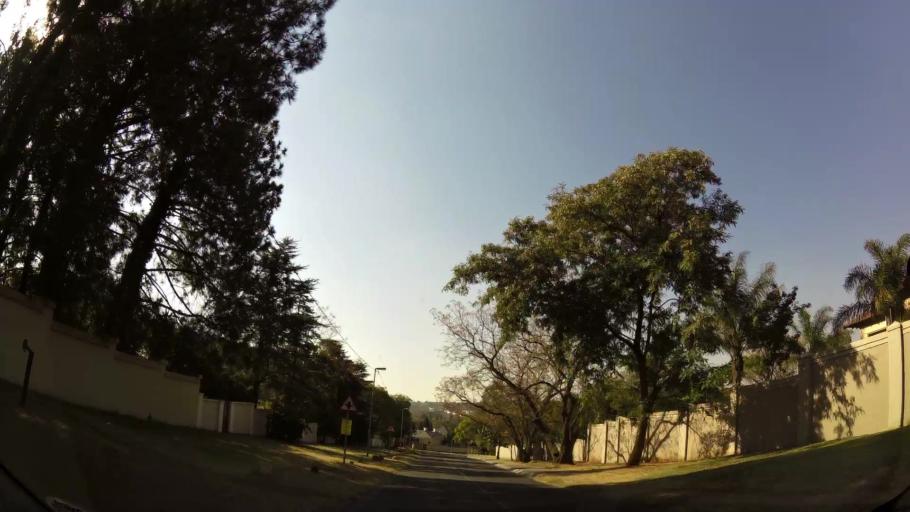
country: ZA
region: Gauteng
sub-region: City of Johannesburg Metropolitan Municipality
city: Diepsloot
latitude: -26.0679
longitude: 28.0068
